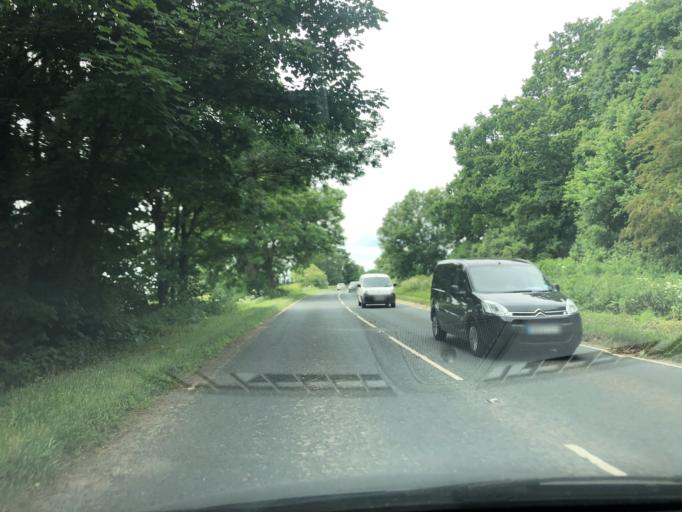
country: GB
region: England
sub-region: North Yorkshire
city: Great Habton
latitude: 54.2608
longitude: -0.8760
